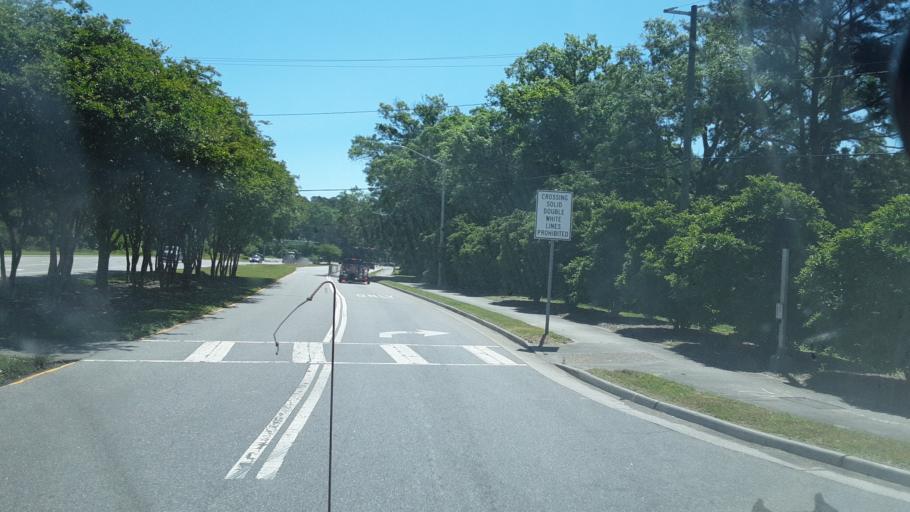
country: US
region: Virginia
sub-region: City of Virginia Beach
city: Virginia Beach
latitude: 36.7942
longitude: -75.9982
